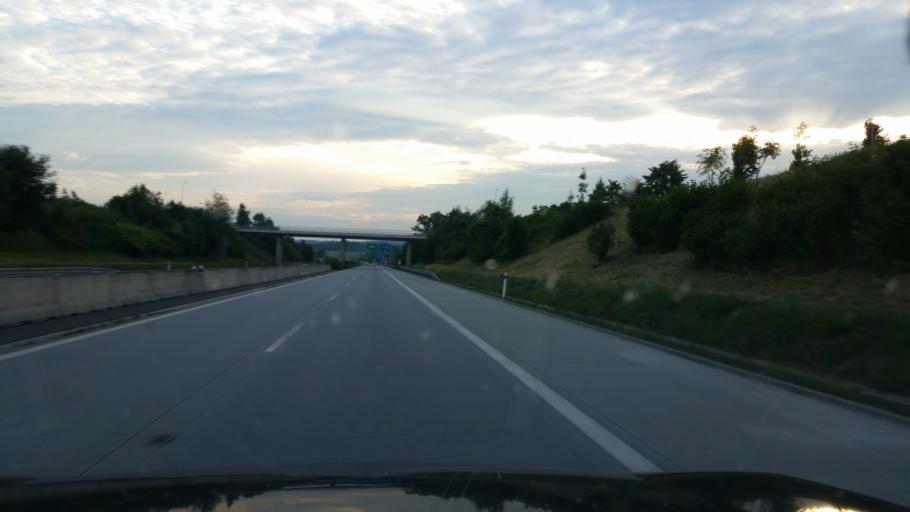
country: CZ
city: Klimkovice
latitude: 49.8004
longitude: 18.1525
